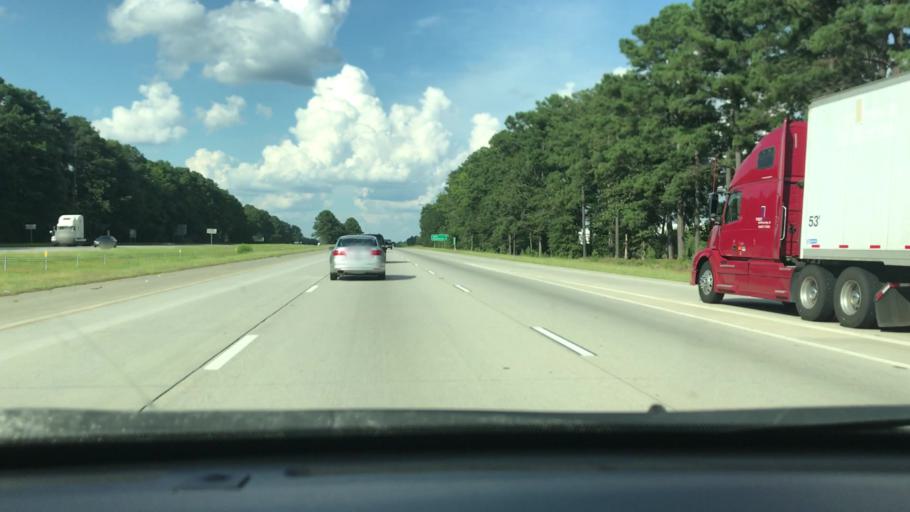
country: US
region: South Carolina
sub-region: Florence County
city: Florence
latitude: 34.2726
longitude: -79.6968
